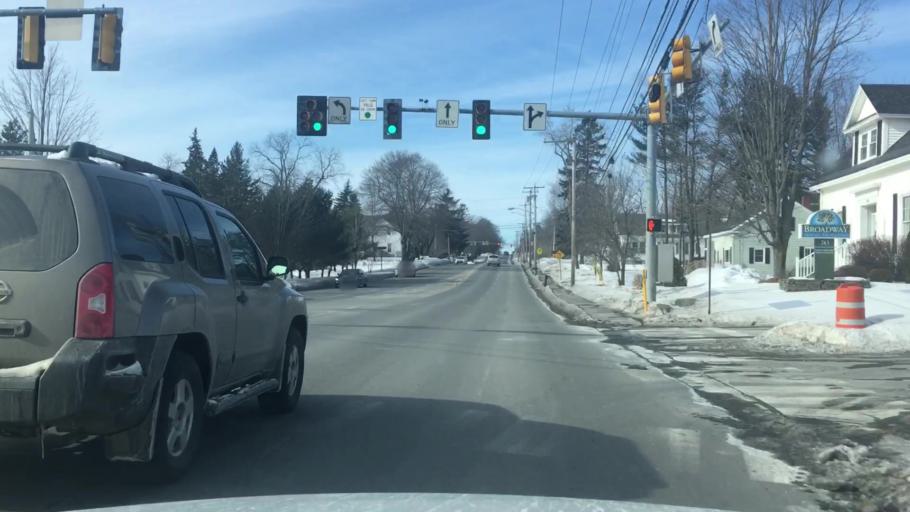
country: US
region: Maine
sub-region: Penobscot County
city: Bangor
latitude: 44.8256
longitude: -68.7813
